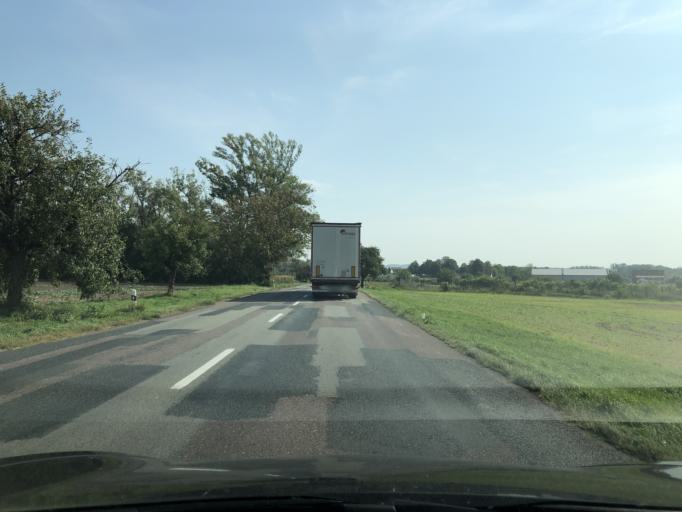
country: CZ
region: South Moravian
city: Brezi
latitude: 48.8220
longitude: 16.5548
